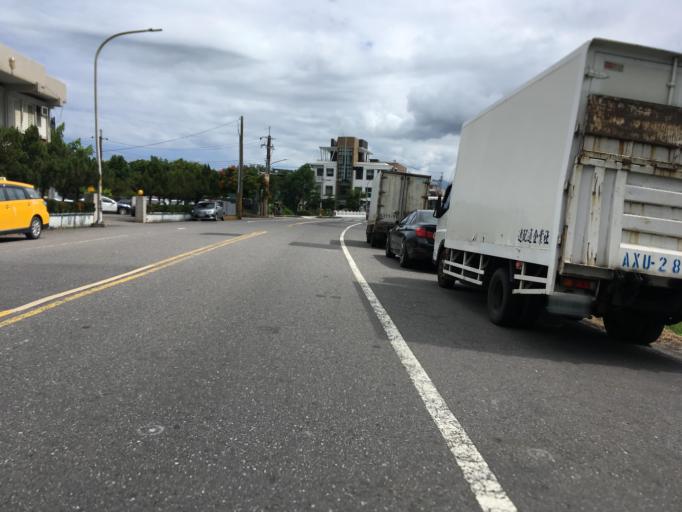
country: TW
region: Taiwan
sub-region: Yilan
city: Yilan
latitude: 24.6878
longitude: 121.7976
